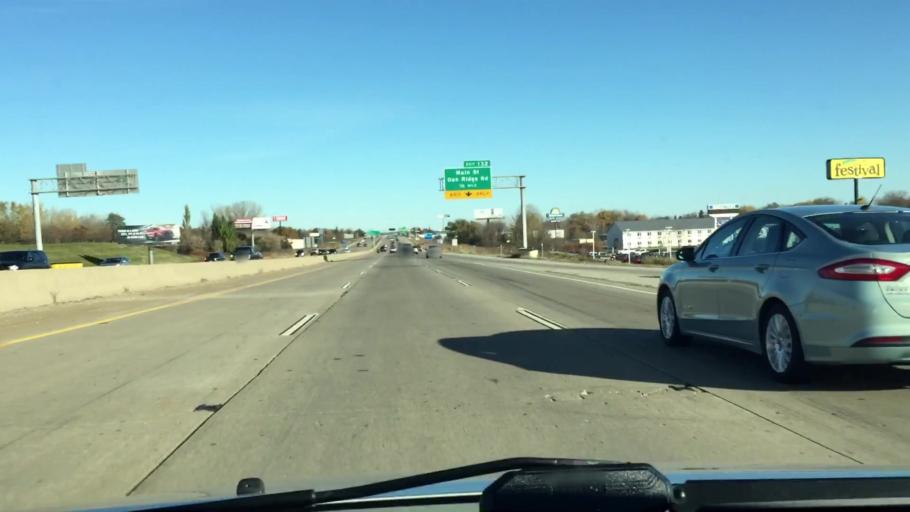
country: US
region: Wisconsin
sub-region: Winnebago County
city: Neenah
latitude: 44.1789
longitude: -88.4887
